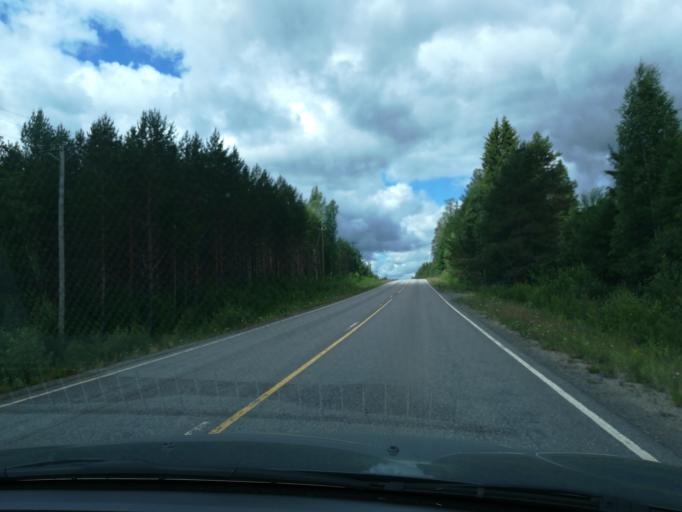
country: FI
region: Southern Savonia
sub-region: Mikkeli
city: Maentyharju
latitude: 61.3646
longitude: 26.9878
